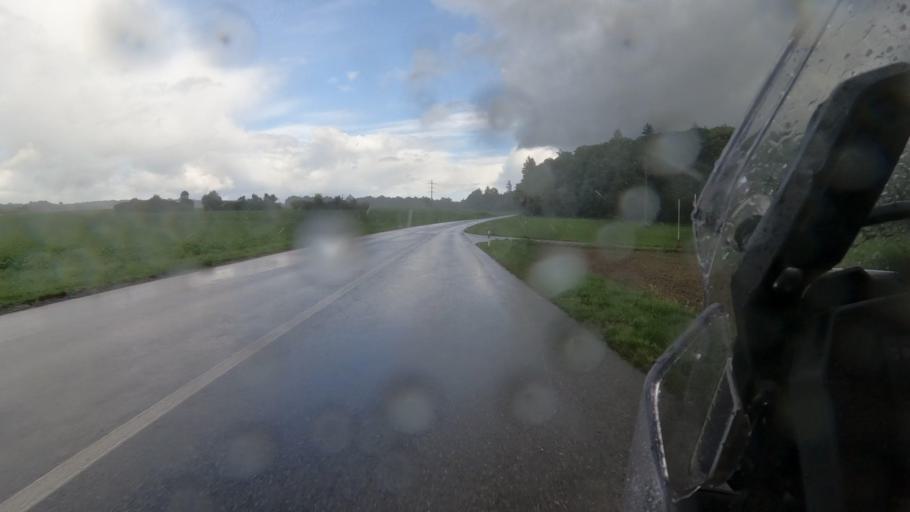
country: CH
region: Zurich
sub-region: Bezirk Andelfingen
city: Marthalen
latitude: 47.6395
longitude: 8.6287
